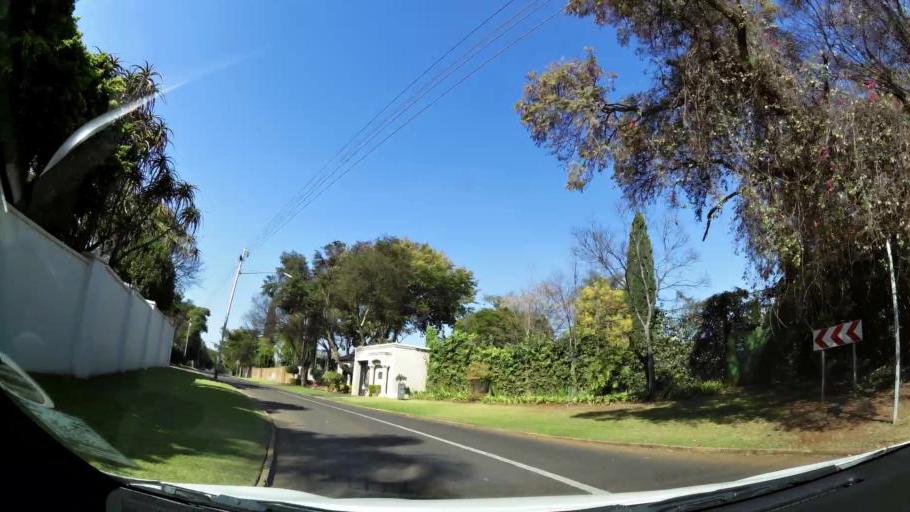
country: ZA
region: Gauteng
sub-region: City of Tshwane Metropolitan Municipality
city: Pretoria
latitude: -25.7612
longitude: 28.2652
